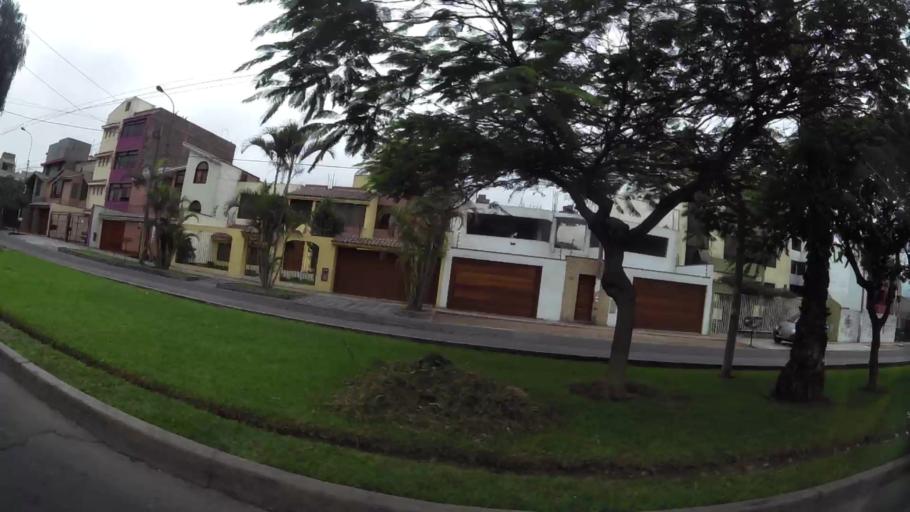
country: PE
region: Lima
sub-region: Lima
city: La Molina
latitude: -12.0718
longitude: -76.9489
